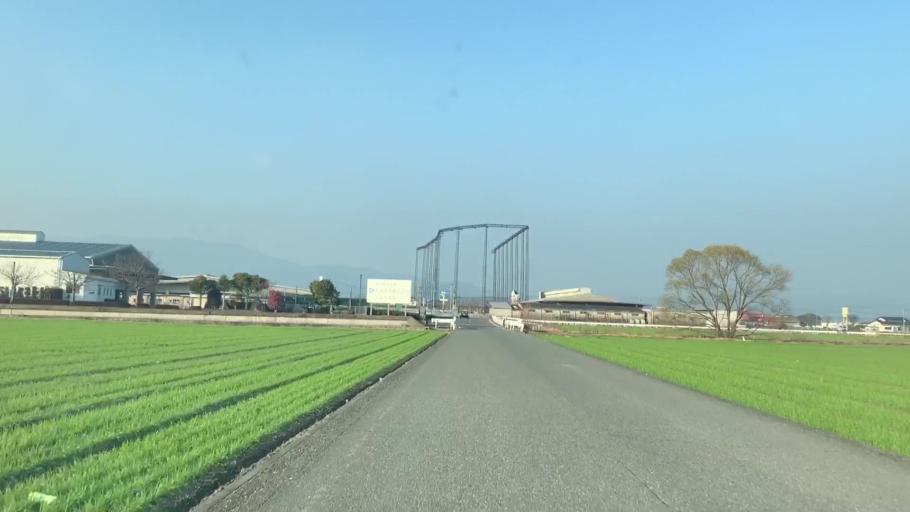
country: JP
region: Saga Prefecture
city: Saga-shi
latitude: 33.2622
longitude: 130.2481
